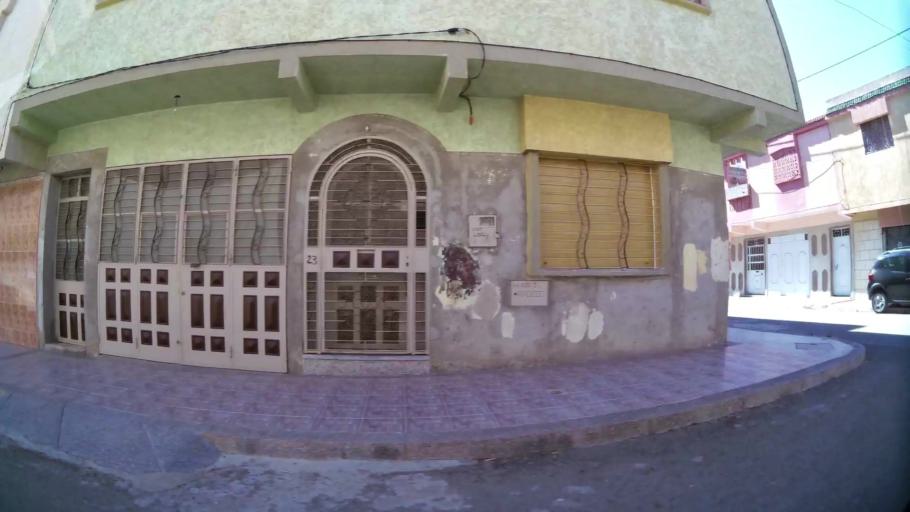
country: MA
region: Oriental
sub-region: Oujda-Angad
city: Oujda
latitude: 34.6535
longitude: -1.9344
